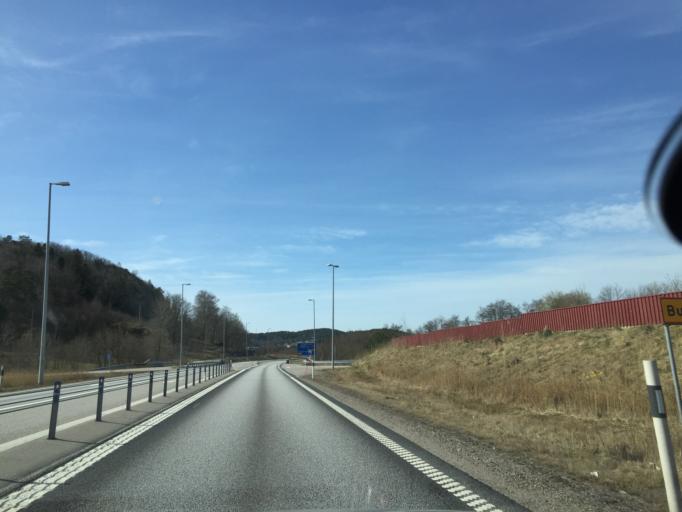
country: SE
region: Vaestra Goetaland
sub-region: Orust
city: Henan
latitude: 58.3452
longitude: 11.7657
